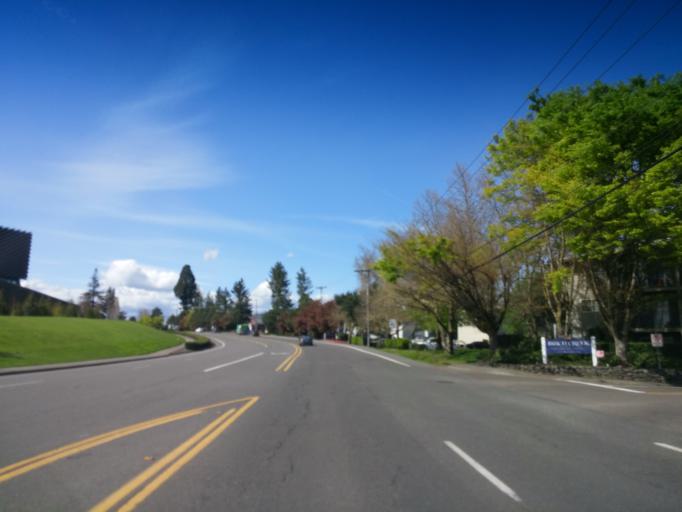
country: US
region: Oregon
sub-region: Washington County
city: Cedar Mill
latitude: 45.5114
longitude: -122.8230
